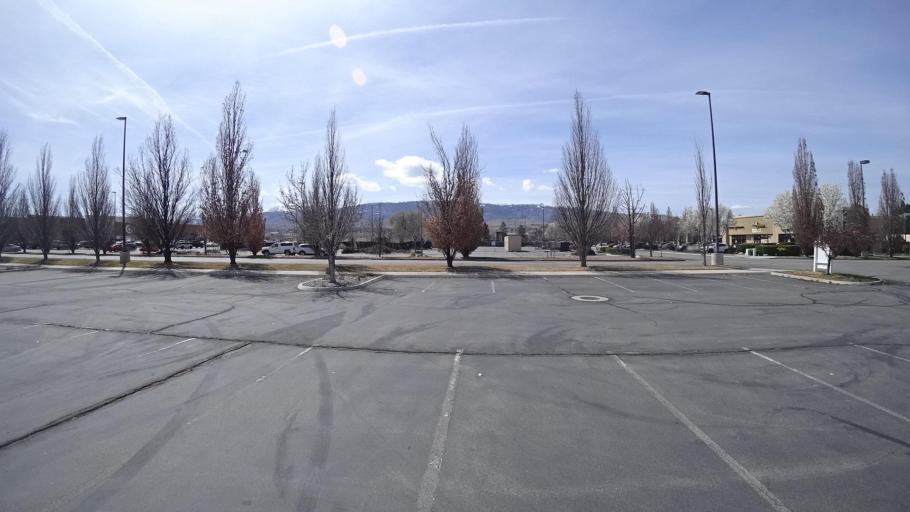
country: US
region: Nevada
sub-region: Washoe County
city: Reno
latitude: 39.4650
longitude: -119.7801
